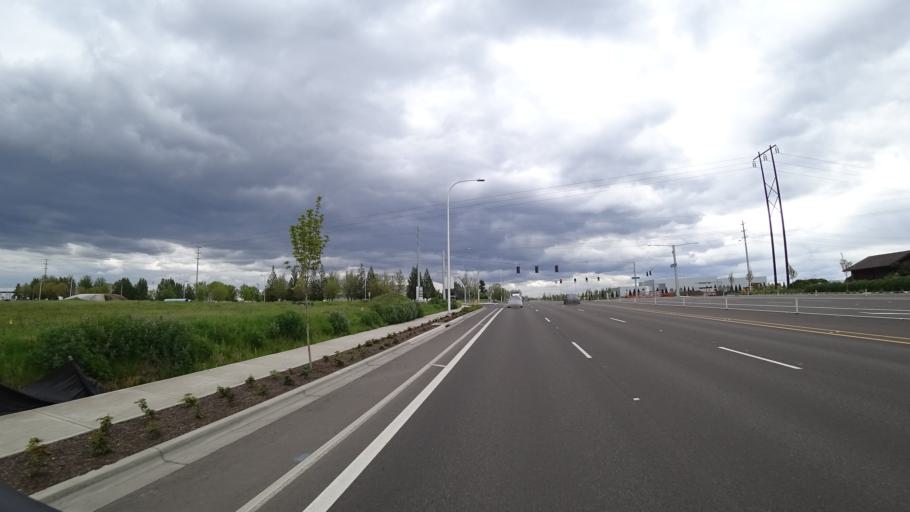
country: US
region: Oregon
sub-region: Washington County
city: Rockcreek
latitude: 45.5579
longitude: -122.9261
